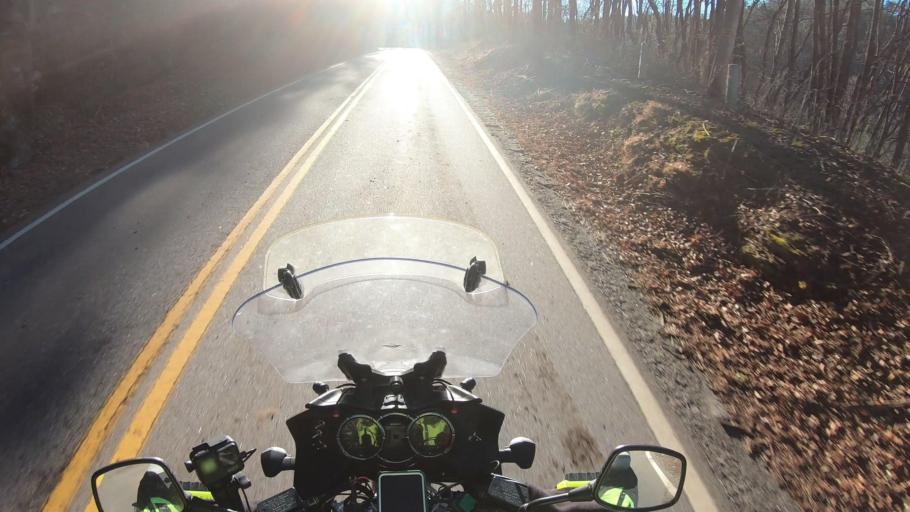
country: US
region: Georgia
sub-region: Union County
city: Blairsville
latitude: 34.7307
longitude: -84.0822
